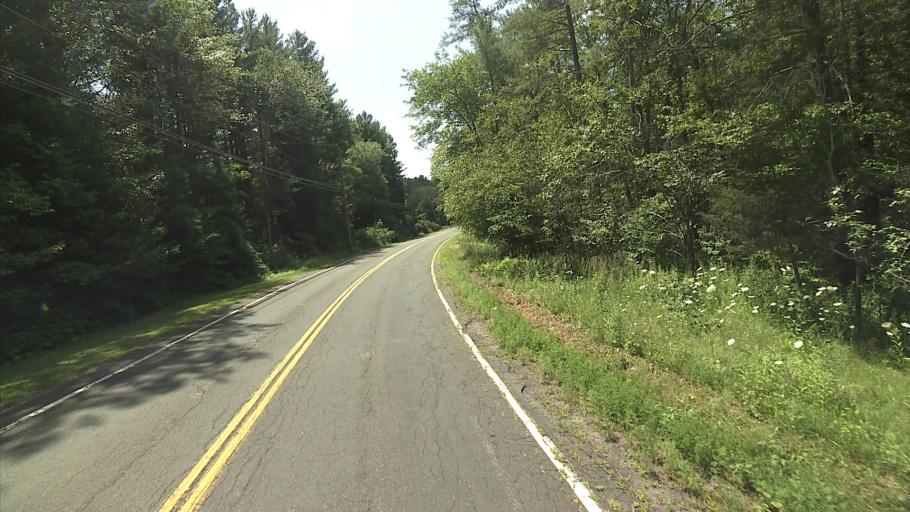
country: US
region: Connecticut
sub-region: Litchfield County
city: West Torrington
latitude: 41.8665
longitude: -73.2946
